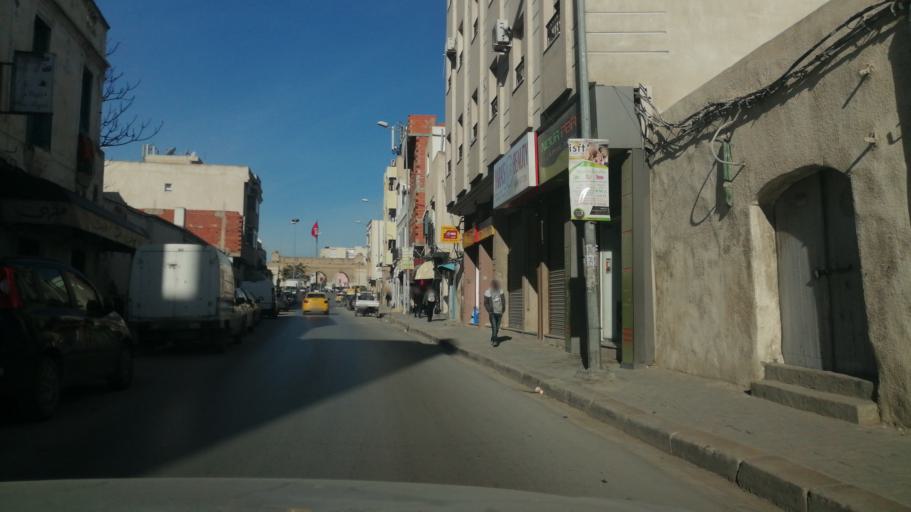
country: TN
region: Tunis
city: Tunis
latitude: 36.8078
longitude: 10.1611
